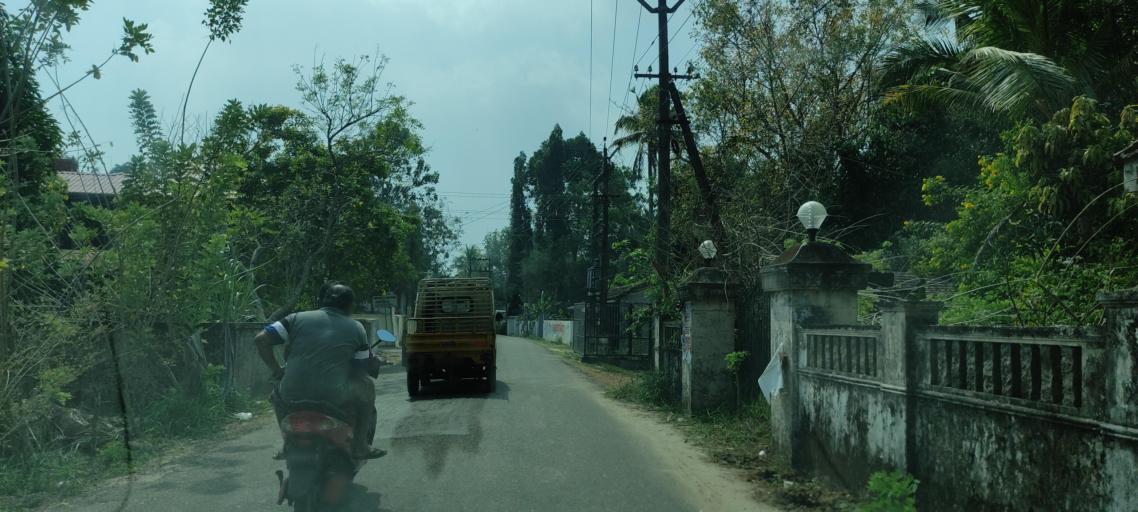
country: IN
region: Kerala
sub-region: Alappuzha
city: Shertallai
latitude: 9.6106
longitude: 76.3473
